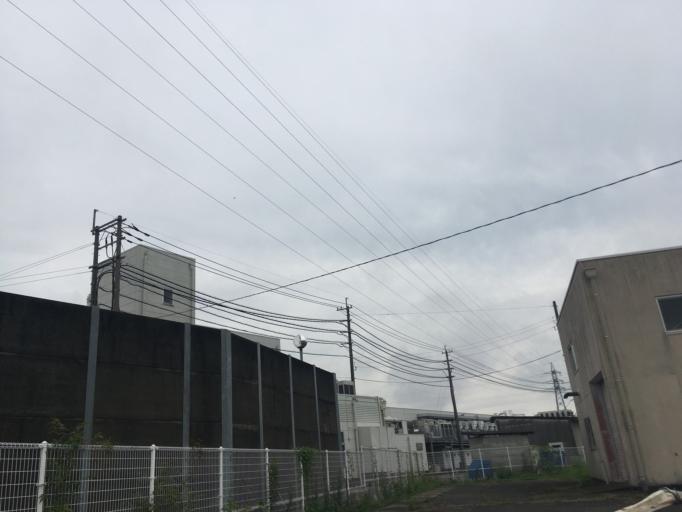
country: JP
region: Saga Prefecture
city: Takeocho-takeo
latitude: 33.2109
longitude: 130.1083
